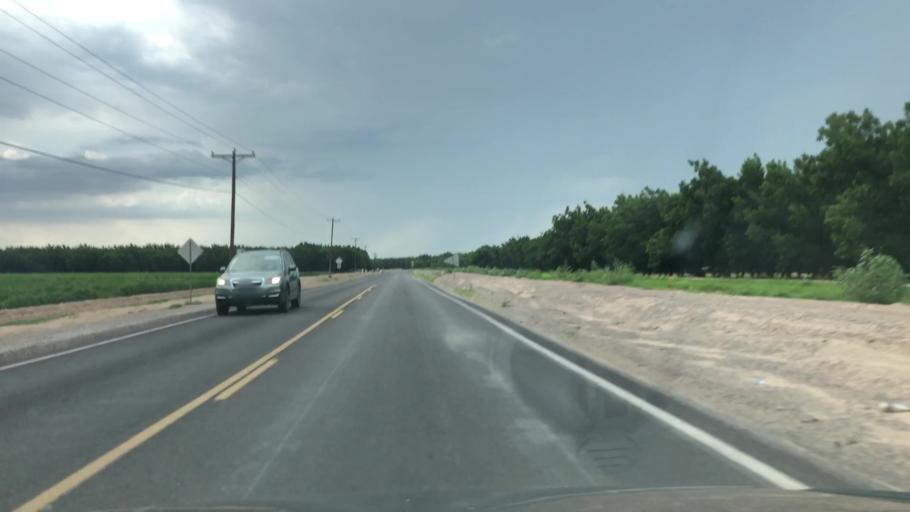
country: US
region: New Mexico
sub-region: Dona Ana County
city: La Union
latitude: 31.9869
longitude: -106.6498
